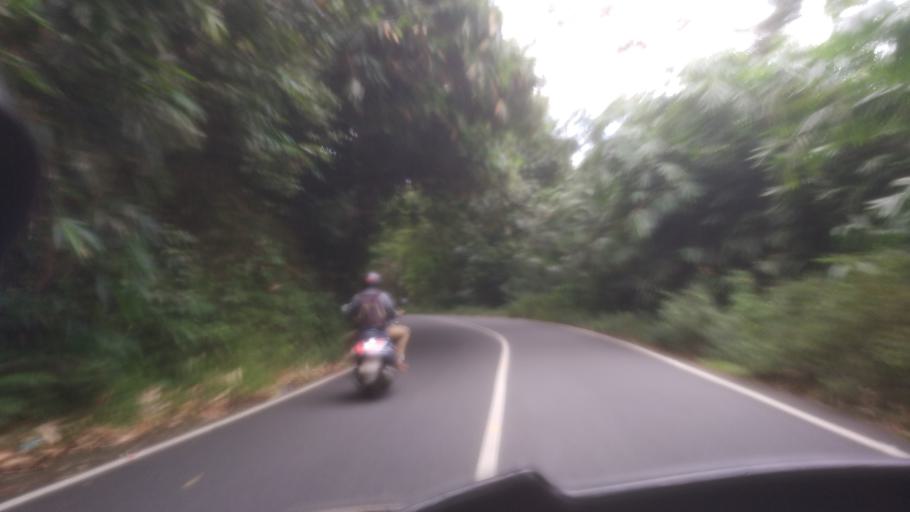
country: IN
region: Kerala
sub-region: Idukki
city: Kuttampuzha
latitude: 10.0615
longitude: 76.8013
